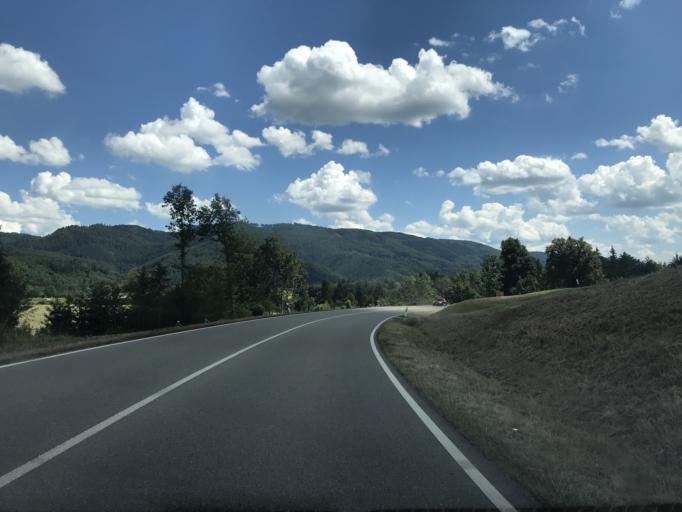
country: DE
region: Baden-Wuerttemberg
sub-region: Freiburg Region
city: Hasel
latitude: 47.6490
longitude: 7.8869
